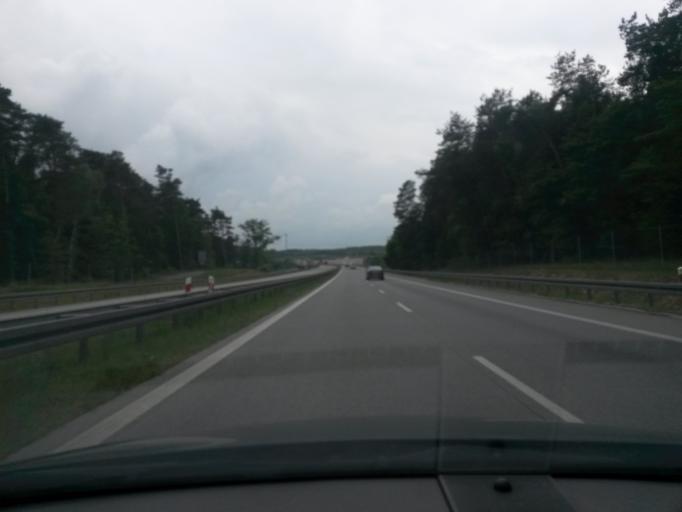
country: PL
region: Lodz Voivodeship
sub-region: Powiat rawski
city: Rawa Mazowiecka
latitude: 51.8291
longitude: 20.3294
